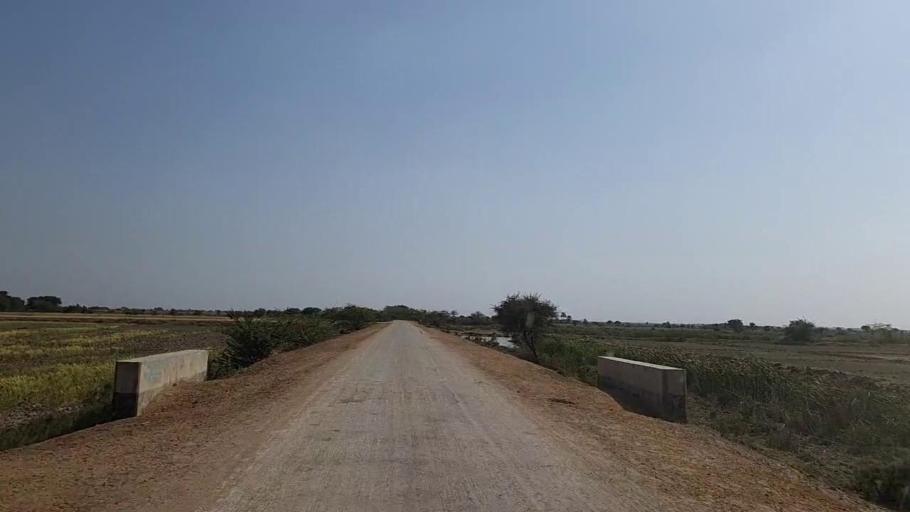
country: PK
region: Sindh
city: Daro Mehar
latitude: 24.7724
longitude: 68.1813
